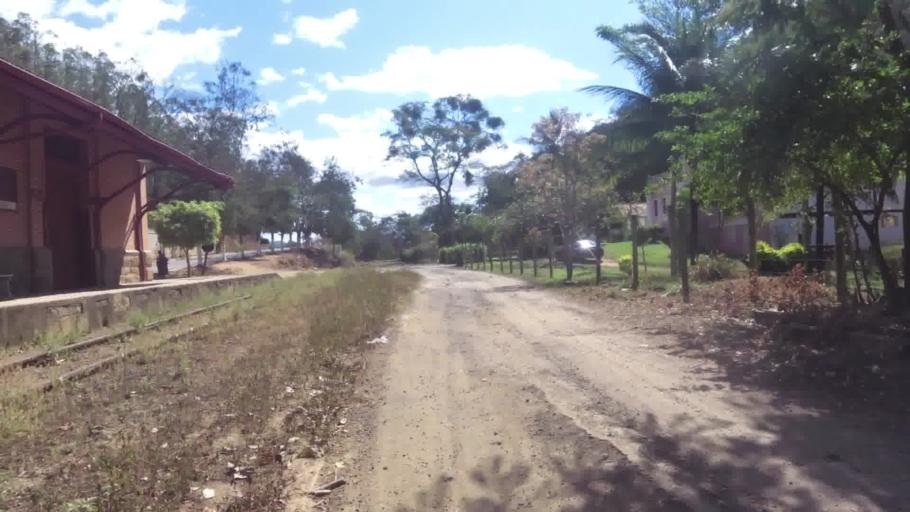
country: BR
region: Espirito Santo
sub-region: Cachoeiro De Itapemirim
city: Cachoeiro de Itapemirim
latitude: -20.9135
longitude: -41.1990
